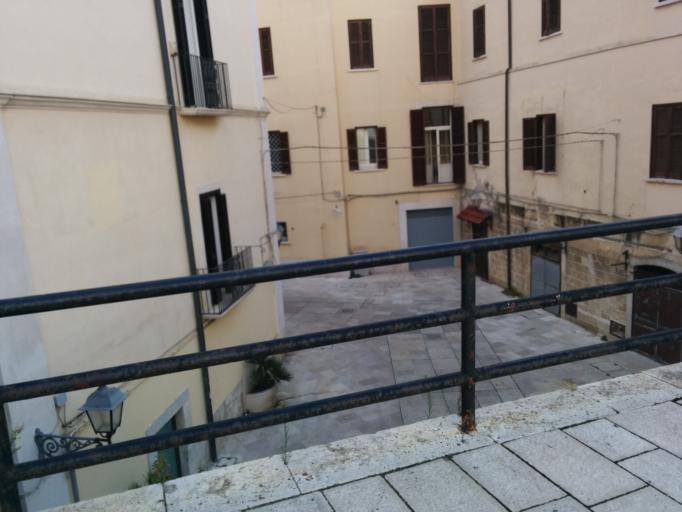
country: IT
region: Apulia
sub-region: Provincia di Bari
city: Bari
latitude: 41.1285
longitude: 16.8726
